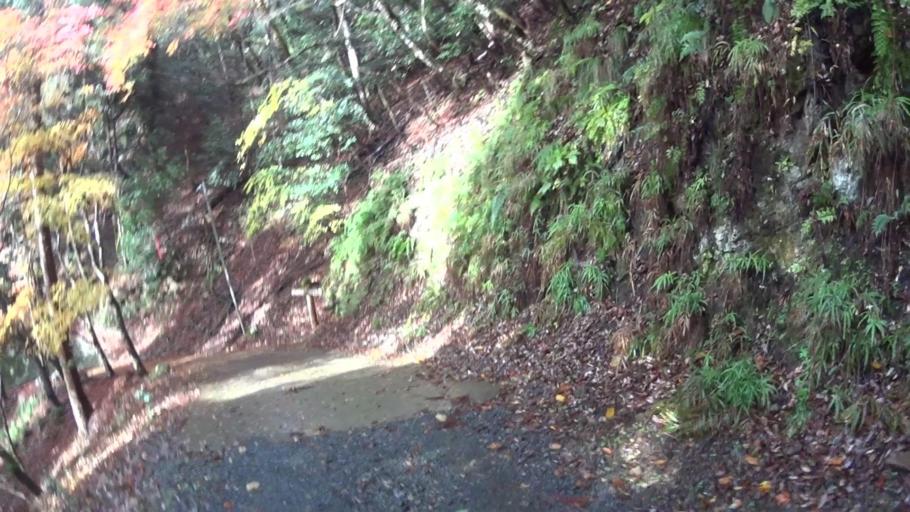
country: JP
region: Kyoto
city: Miyazu
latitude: 35.4311
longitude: 135.1522
